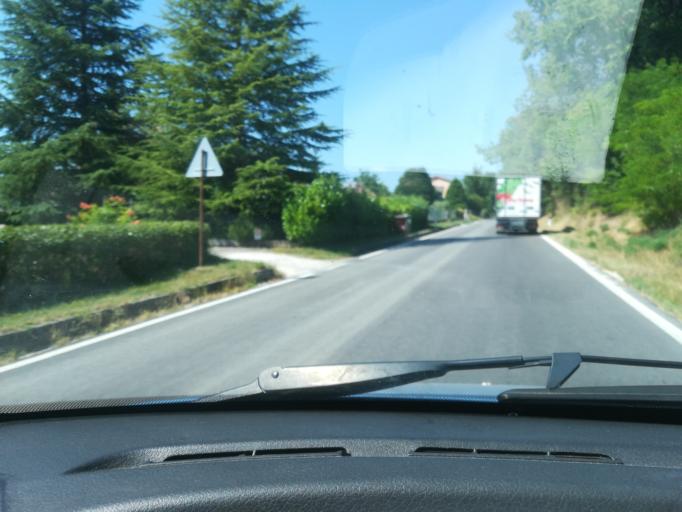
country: IT
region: The Marches
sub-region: Provincia di Macerata
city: Ripe San Ginesio
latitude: 43.1147
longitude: 13.3686
